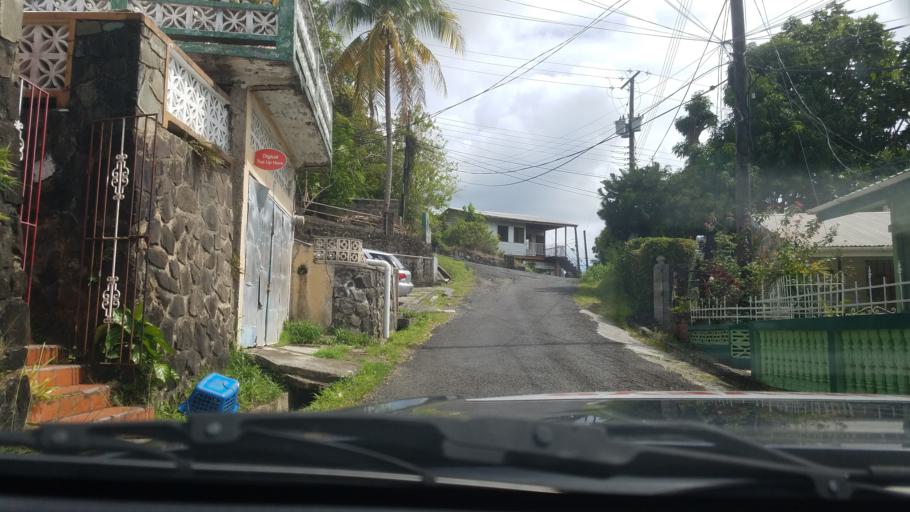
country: LC
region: Castries Quarter
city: Bisee
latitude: 14.0139
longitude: -60.9795
